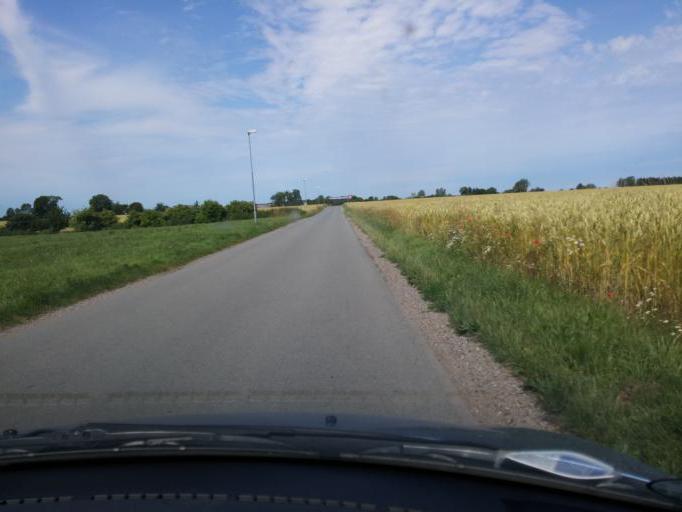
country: DK
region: South Denmark
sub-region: Kerteminde Kommune
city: Langeskov
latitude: 55.4052
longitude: 10.6059
